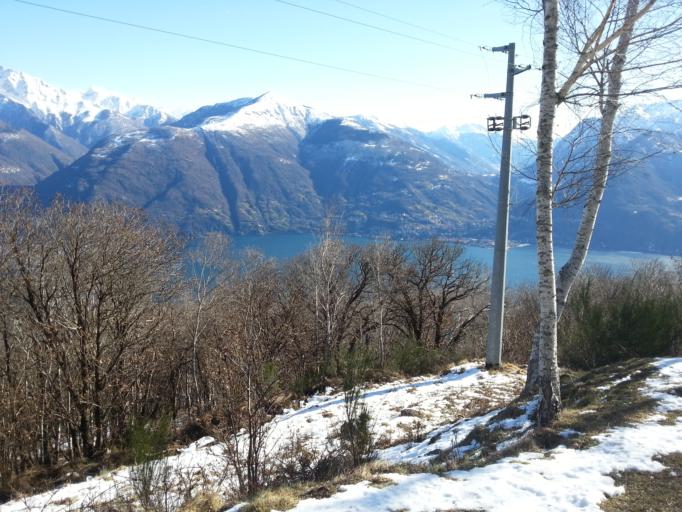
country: IT
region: Lombardy
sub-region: Provincia di Como
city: San Siro
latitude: 46.0655
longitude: 9.2484
